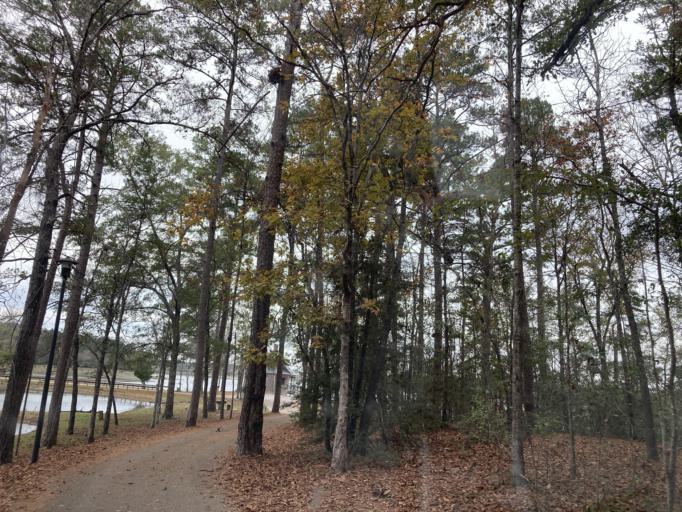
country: US
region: Mississippi
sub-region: Lamar County
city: Lumberton
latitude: 31.0830
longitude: -89.4974
